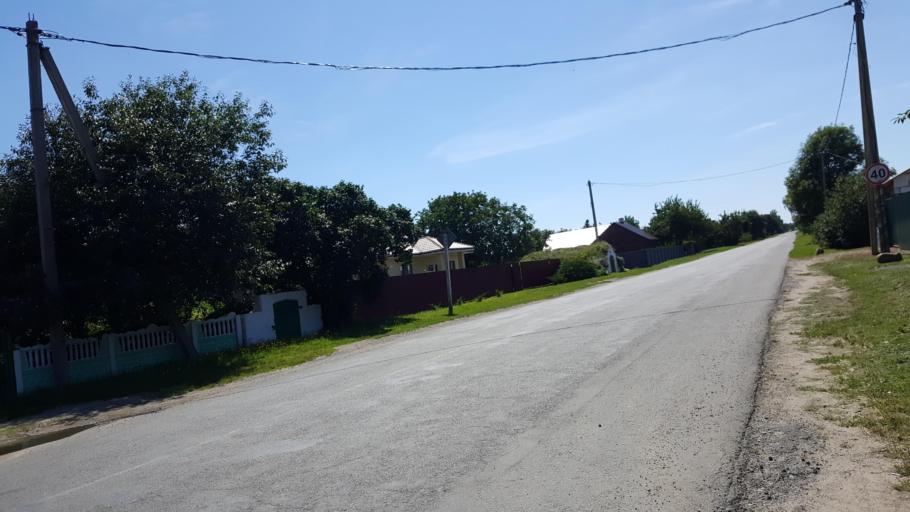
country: BY
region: Brest
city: Charnawchytsy
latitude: 52.2663
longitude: 23.5827
